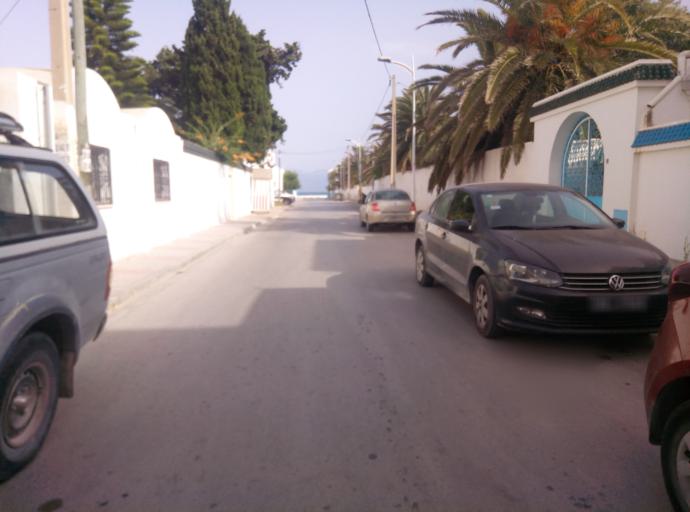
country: TN
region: Nabul
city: Al Hammamat
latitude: 36.3949
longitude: 10.6173
